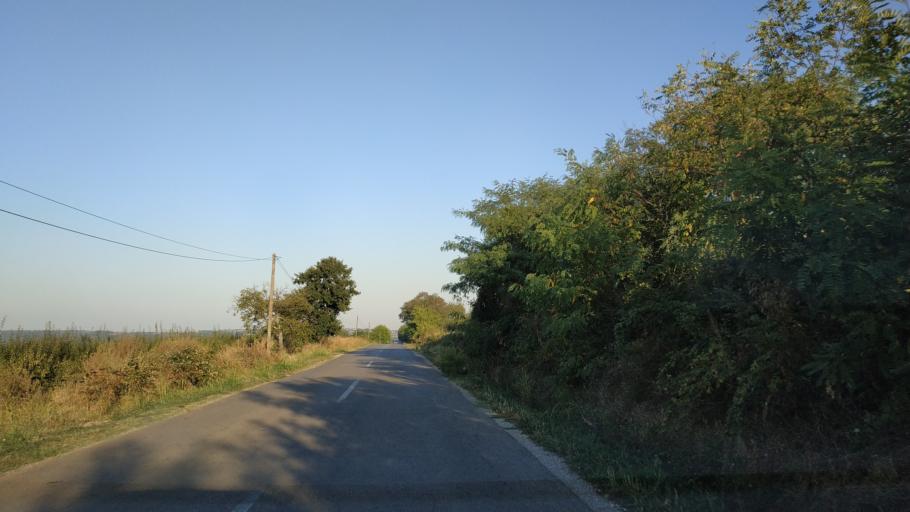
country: RS
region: Central Serbia
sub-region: Sumadijski Okrug
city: Topola
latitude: 44.2718
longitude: 20.6416
